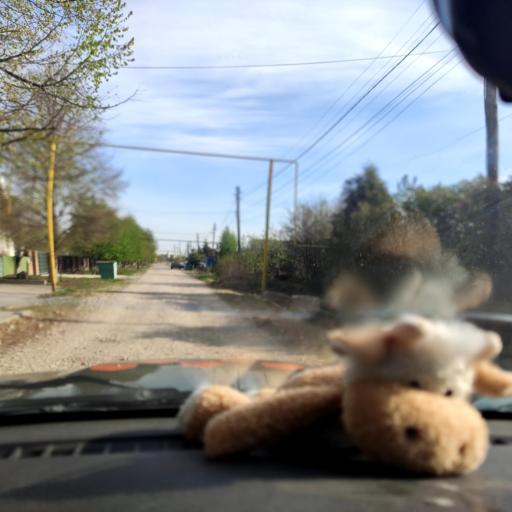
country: RU
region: Samara
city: Tol'yatti
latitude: 53.5716
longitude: 49.3079
